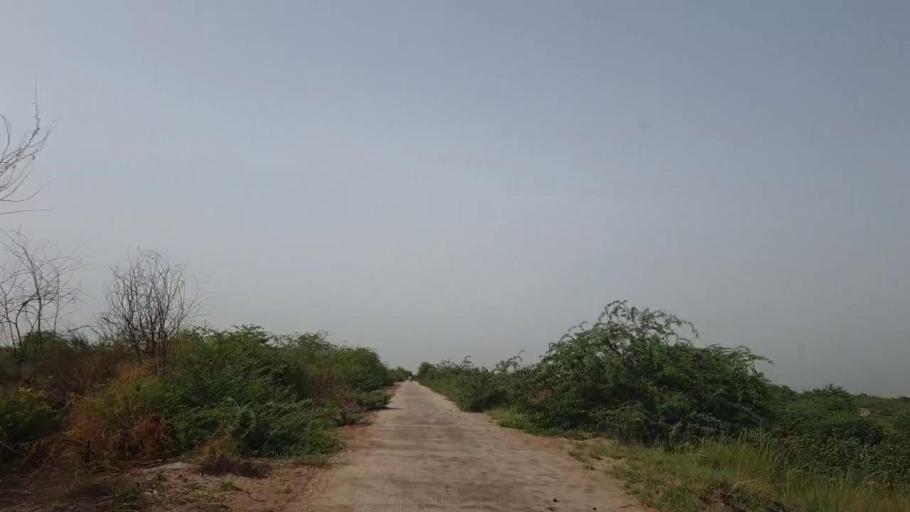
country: PK
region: Sindh
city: Nawabshah
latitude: 26.1128
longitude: 68.4398
